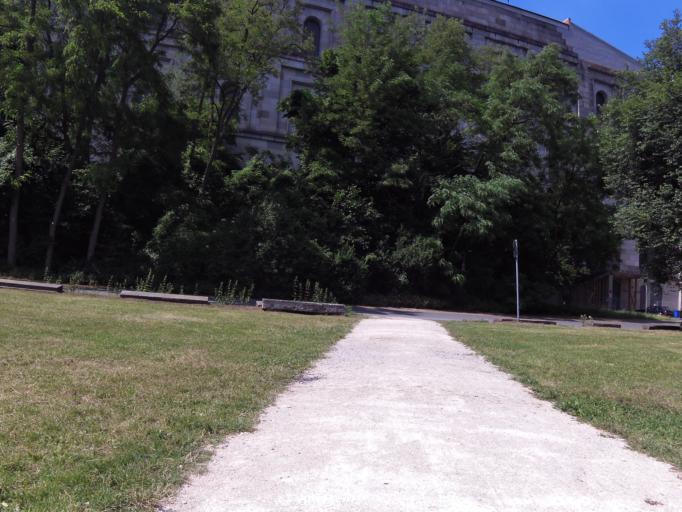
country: DE
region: Bavaria
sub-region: Regierungsbezirk Mittelfranken
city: Nuernberg
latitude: 49.4312
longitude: 11.1140
